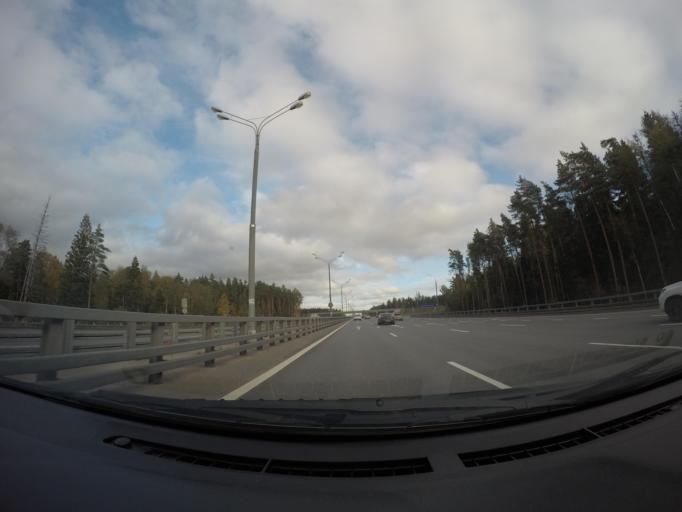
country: RU
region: Moskovskaya
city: Krasnoznamensk
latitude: 55.6083
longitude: 37.0476
